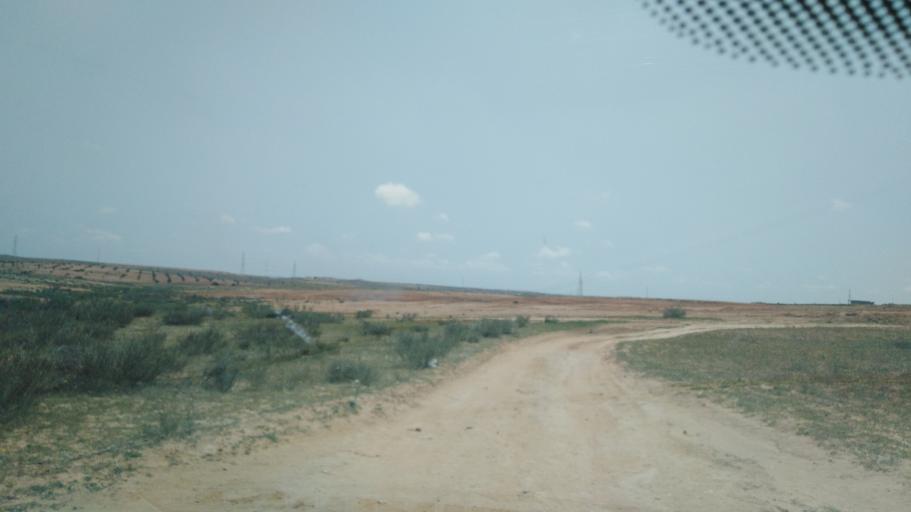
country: TN
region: Safaqis
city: Sfax
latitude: 34.7716
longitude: 10.5782
